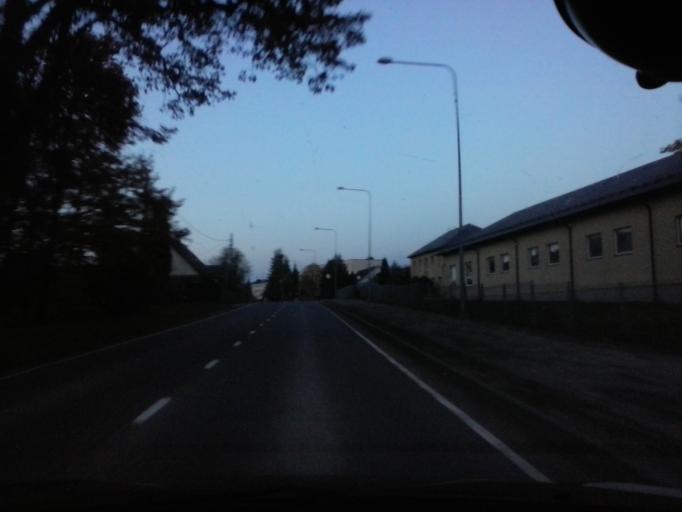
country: EE
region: Raplamaa
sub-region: Rapla vald
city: Rapla
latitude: 58.9965
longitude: 24.7899
